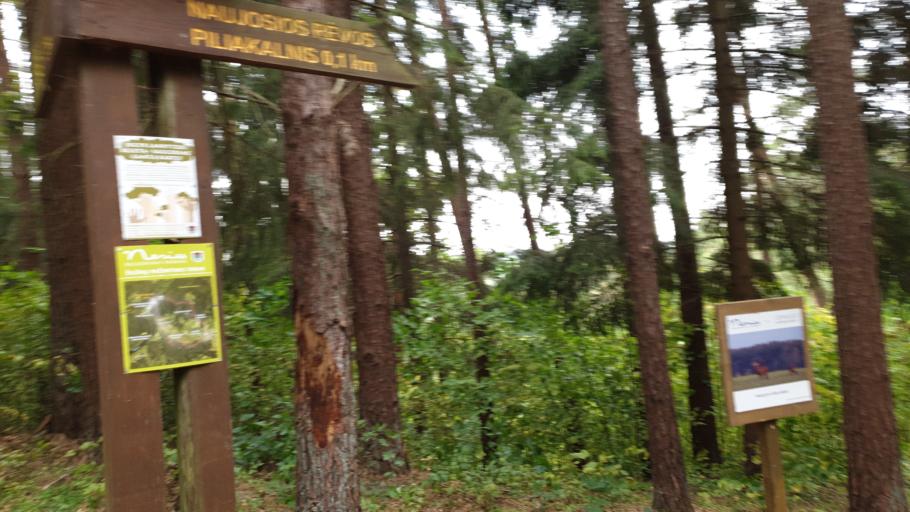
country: LT
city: Grigiskes
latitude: 54.7400
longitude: 25.0248
